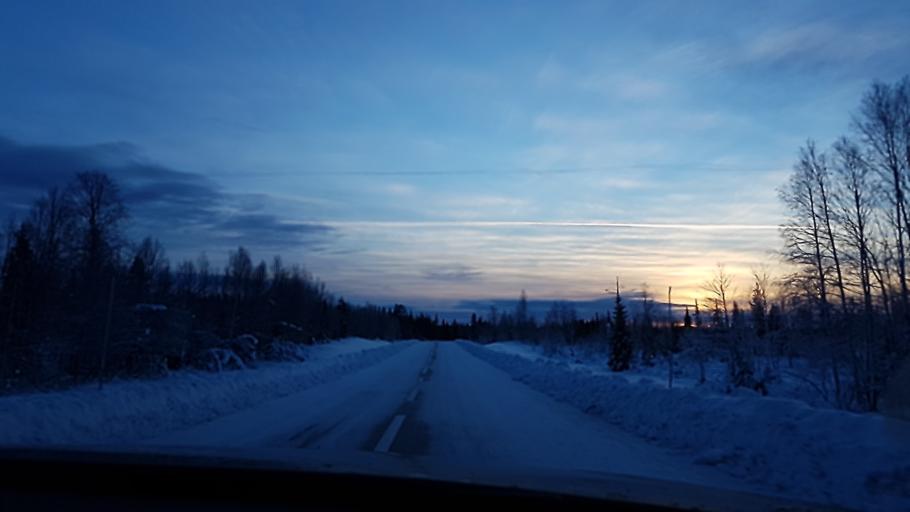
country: SE
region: Norrbotten
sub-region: Jokkmokks Kommun
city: Jokkmokk
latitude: 66.1095
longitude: 20.0507
